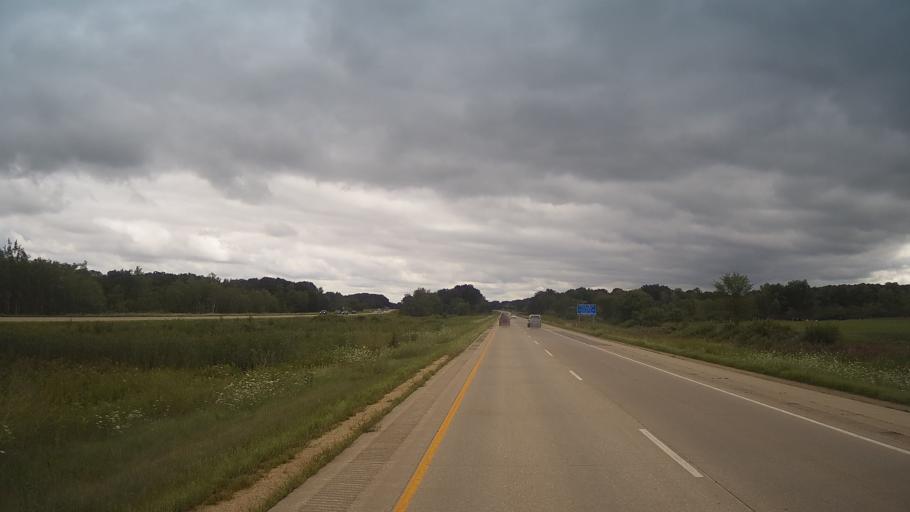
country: US
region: Wisconsin
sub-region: Monroe County
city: Sparta
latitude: 43.9049
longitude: -90.8961
